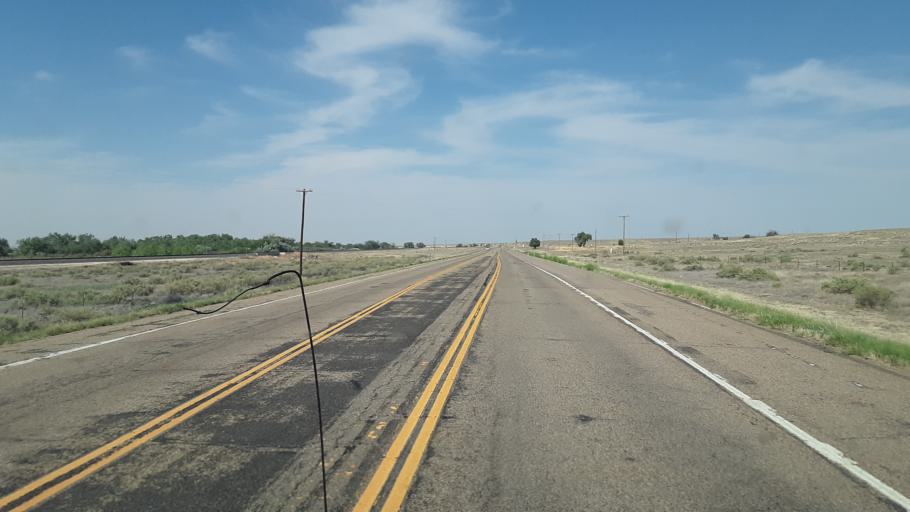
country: US
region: Colorado
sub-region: Otero County
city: La Junta
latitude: 38.0367
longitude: -103.4056
